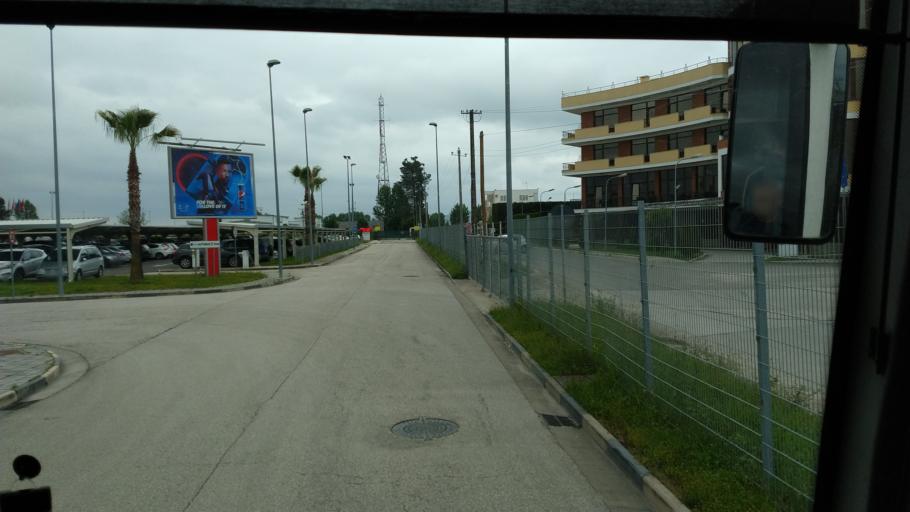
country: AL
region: Tirane
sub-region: Rrethi i Tiranes
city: Preze
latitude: 41.4171
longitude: 19.7129
